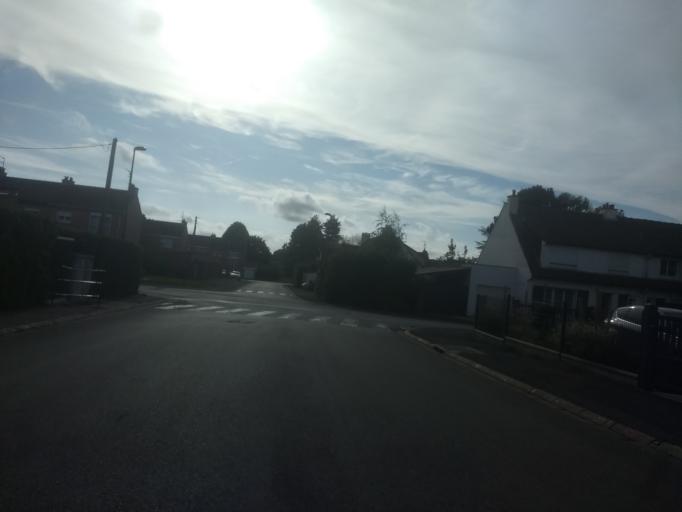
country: FR
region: Nord-Pas-de-Calais
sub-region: Departement du Pas-de-Calais
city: Dainville
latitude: 50.2875
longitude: 2.7324
